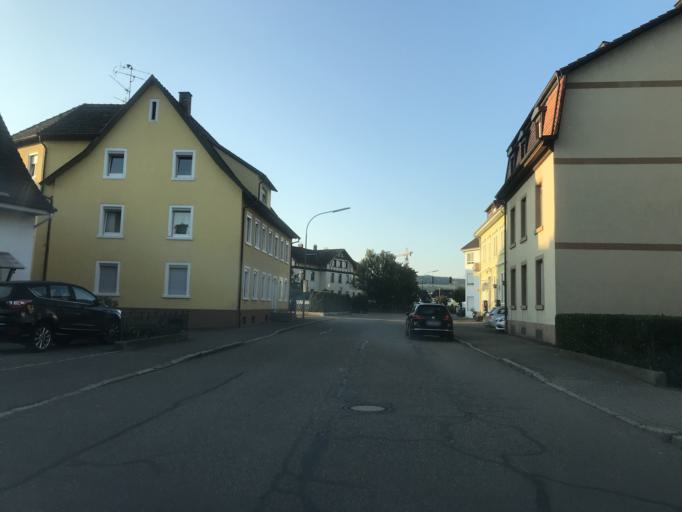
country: DE
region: Baden-Wuerttemberg
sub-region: Freiburg Region
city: Schopfheim
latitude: 47.6597
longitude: 7.8340
